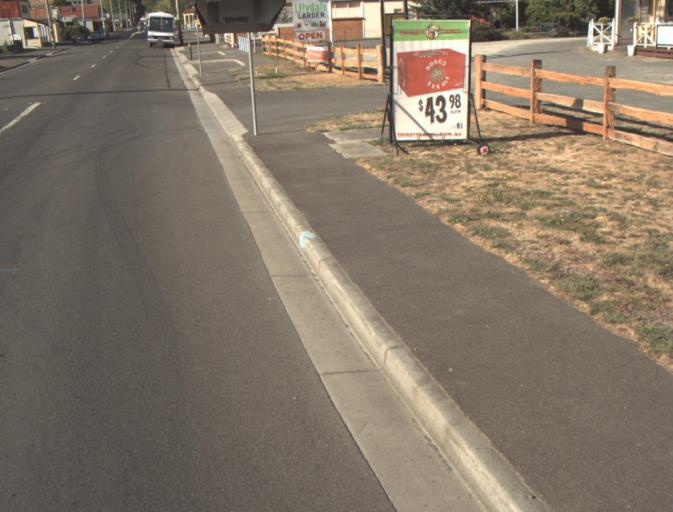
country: AU
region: Tasmania
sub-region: Launceston
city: Mayfield
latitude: -41.2490
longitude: 147.2178
